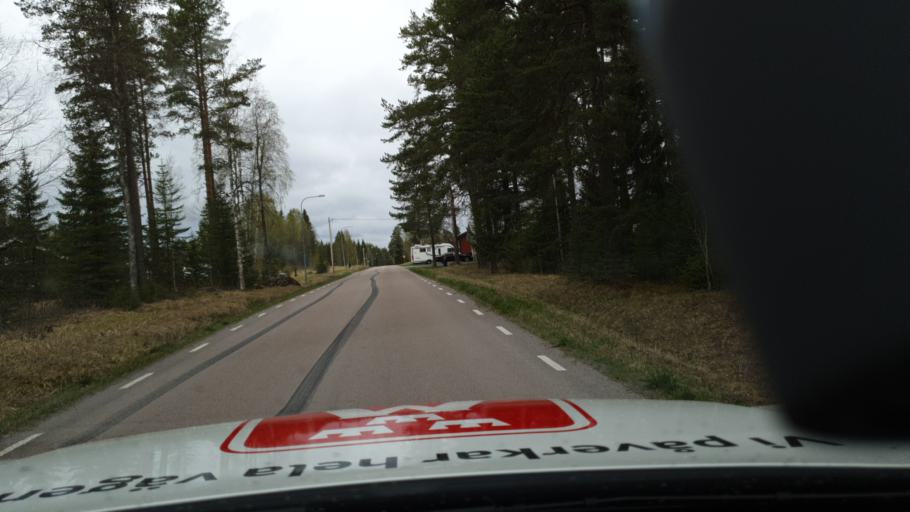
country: SE
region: Jaemtland
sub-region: OEstersunds Kommun
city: Lit
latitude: 63.2964
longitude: 14.9764
